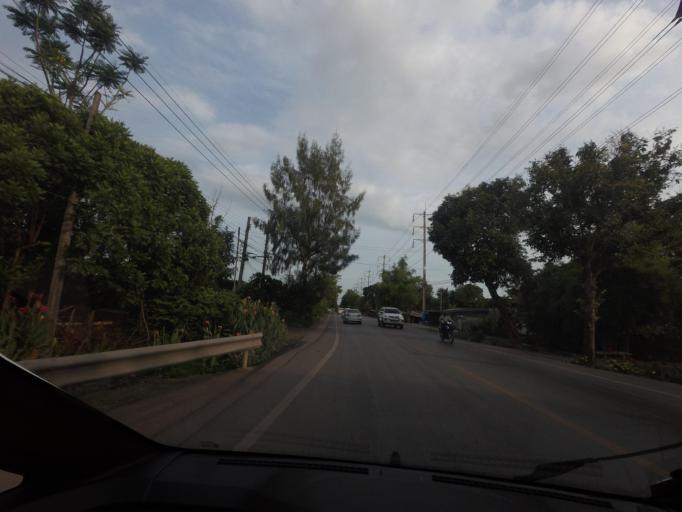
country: TH
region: Bangkok
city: Nong Chok
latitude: 13.8960
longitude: 100.8629
